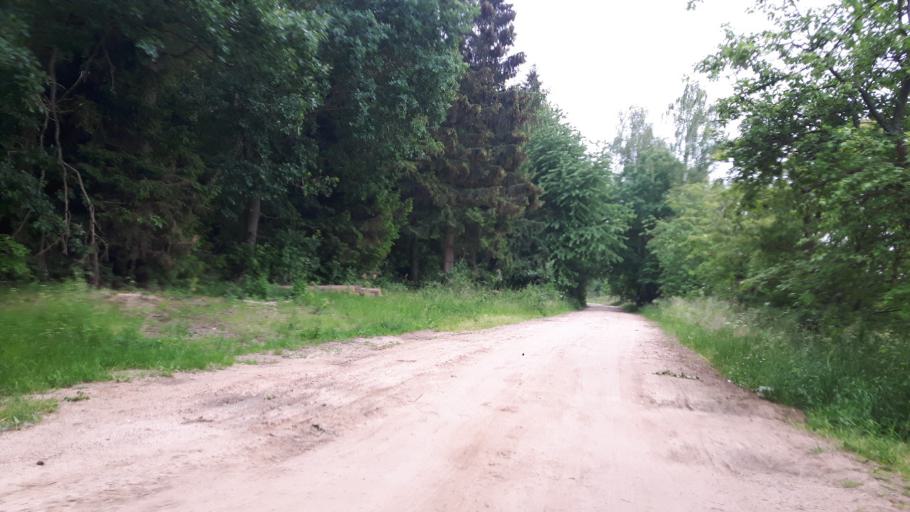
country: PL
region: Warmian-Masurian Voivodeship
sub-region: Powiat elblaski
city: Tolkmicko
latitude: 54.3202
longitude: 19.6080
